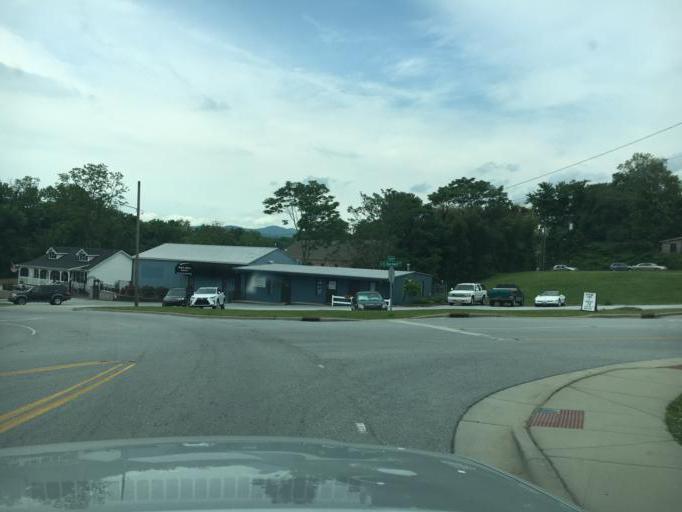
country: US
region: North Carolina
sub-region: Henderson County
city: Hendersonville
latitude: 35.3129
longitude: -82.4570
